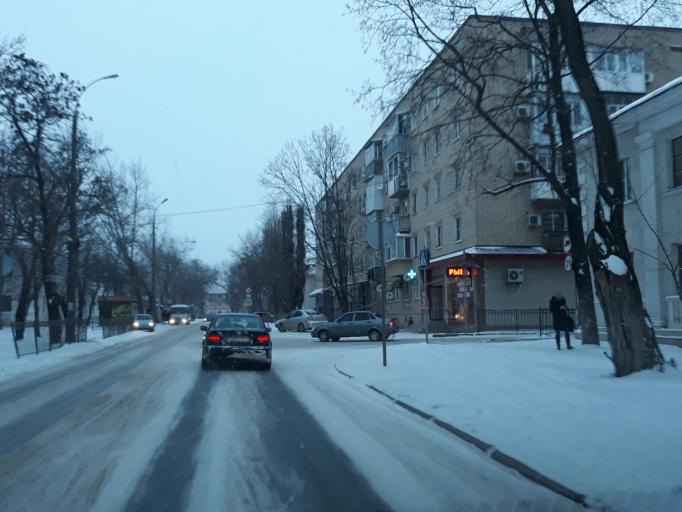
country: RU
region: Rostov
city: Taganrog
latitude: 47.2616
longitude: 38.9389
